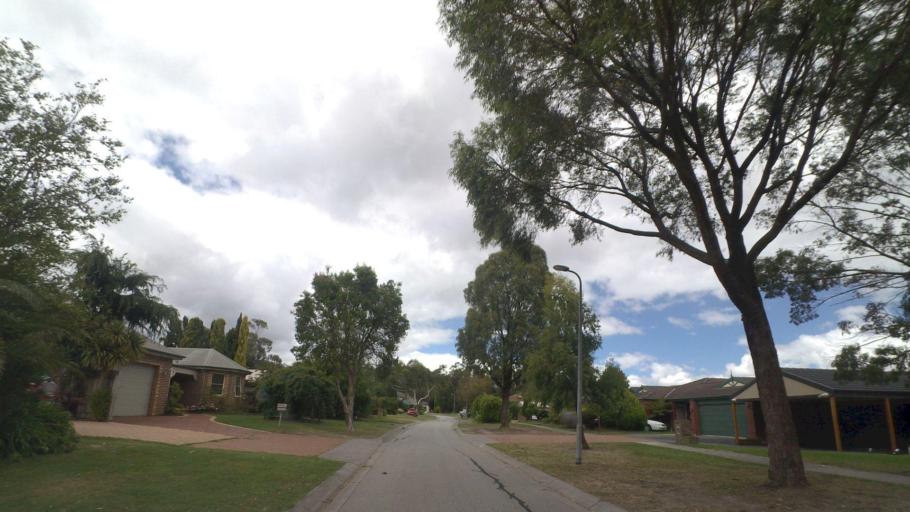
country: AU
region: Victoria
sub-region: Knox
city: The Basin
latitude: -37.8395
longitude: 145.3086
